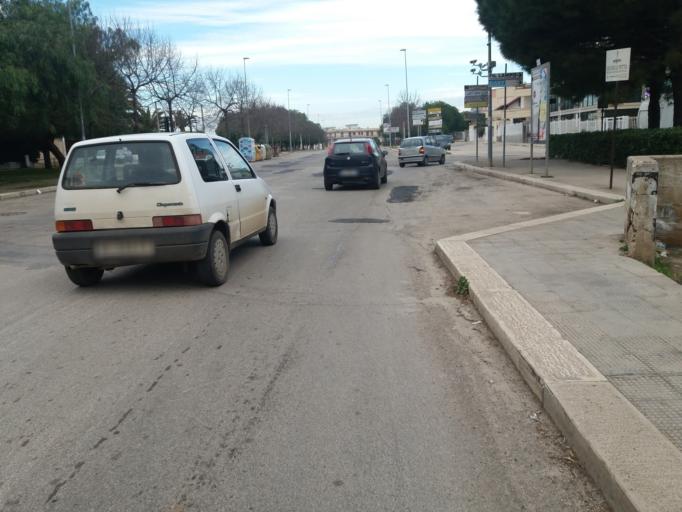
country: IT
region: Apulia
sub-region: Provincia di Bari
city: Bitonto
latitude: 41.1129
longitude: 16.6829
